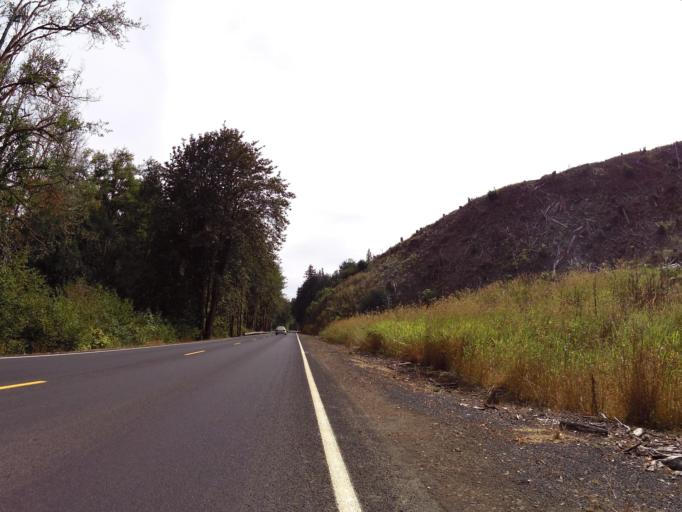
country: US
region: Washington
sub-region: Cowlitz County
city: Castle Rock
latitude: 46.3430
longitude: -122.9388
